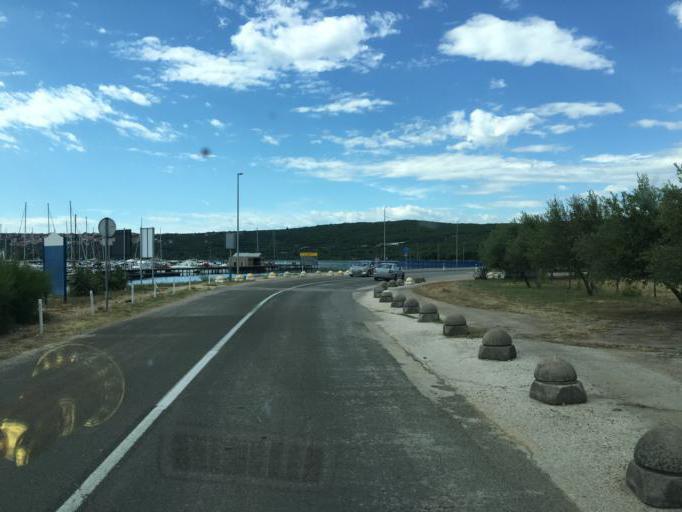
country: HR
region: Primorsko-Goranska
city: Punat
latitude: 45.0328
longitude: 14.6292
